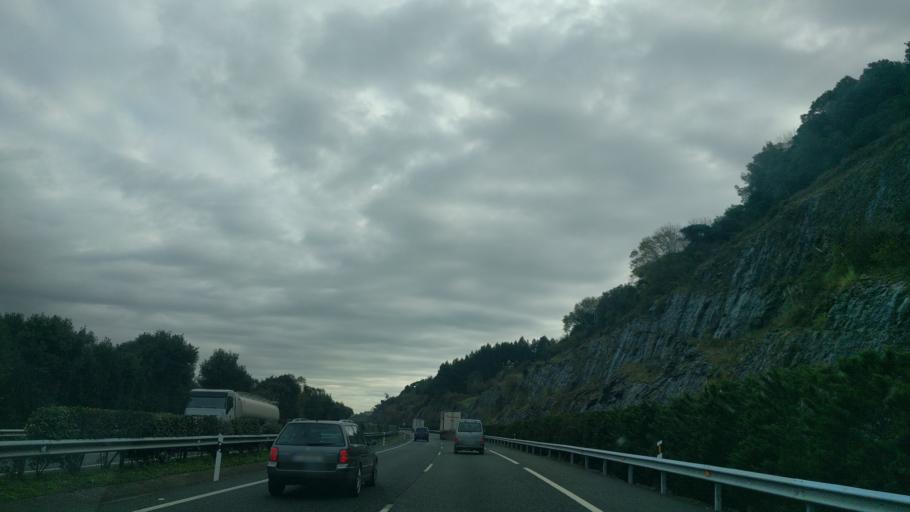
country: ES
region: Cantabria
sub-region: Provincia de Cantabria
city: Castro-Urdiales
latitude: 43.3979
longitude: -3.2755
